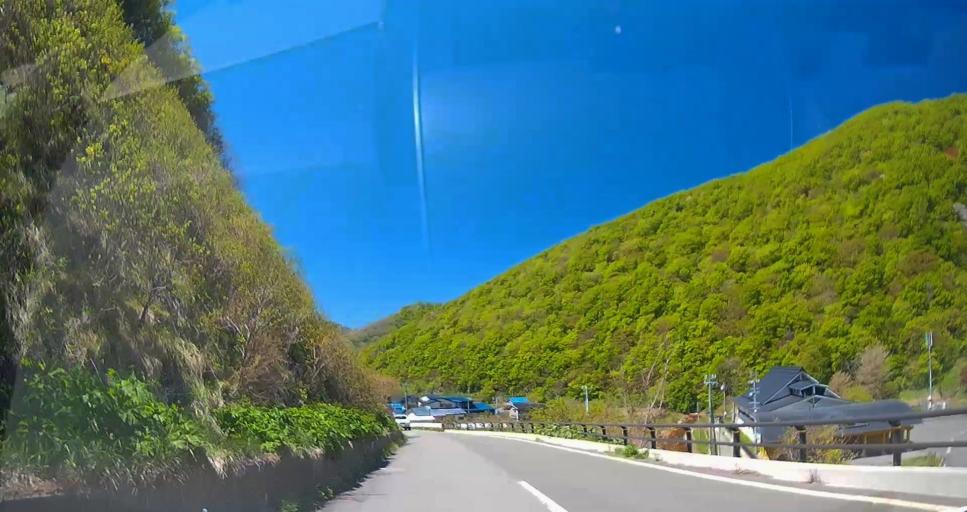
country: JP
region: Aomori
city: Mutsu
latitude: 41.3267
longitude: 140.8136
